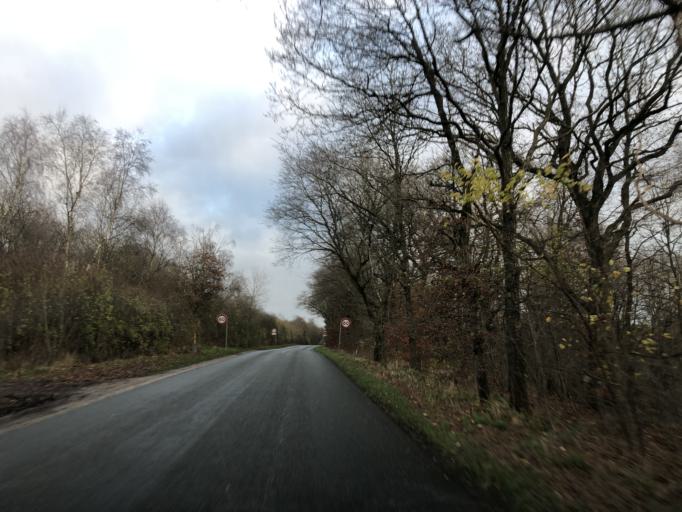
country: DK
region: Central Jutland
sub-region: Viborg Kommune
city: Viborg
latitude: 56.4750
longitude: 9.3523
